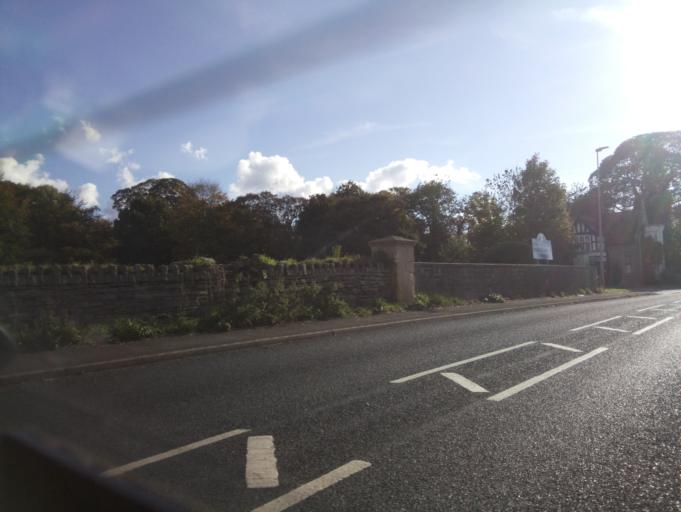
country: GB
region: Wales
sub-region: Sir Powys
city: Hay
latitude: 52.0298
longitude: -3.2084
